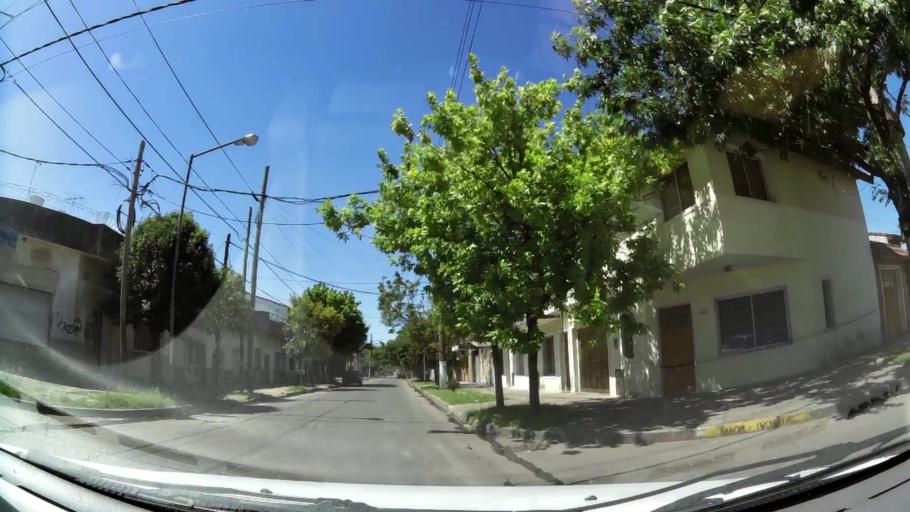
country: AR
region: Buenos Aires
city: Caseros
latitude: -34.5698
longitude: -58.5709
